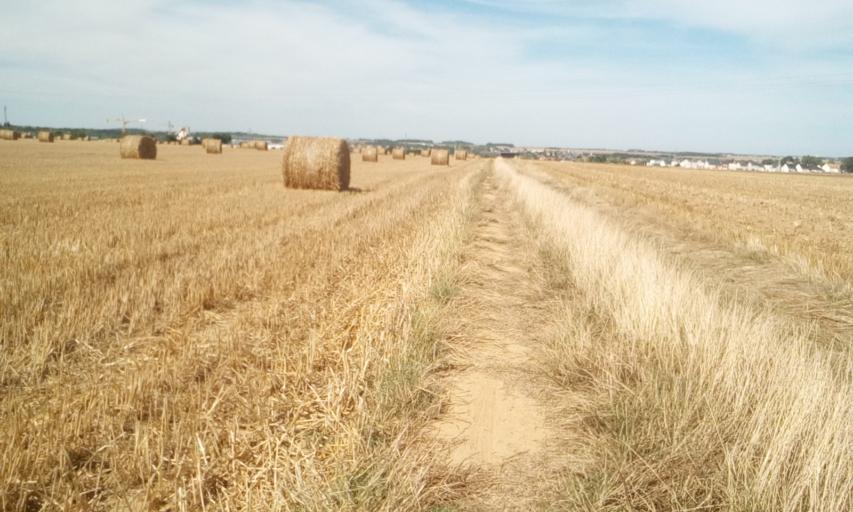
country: FR
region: Lower Normandy
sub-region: Departement du Calvados
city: Fontaine-Etoupefour
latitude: 49.1327
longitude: -0.4546
